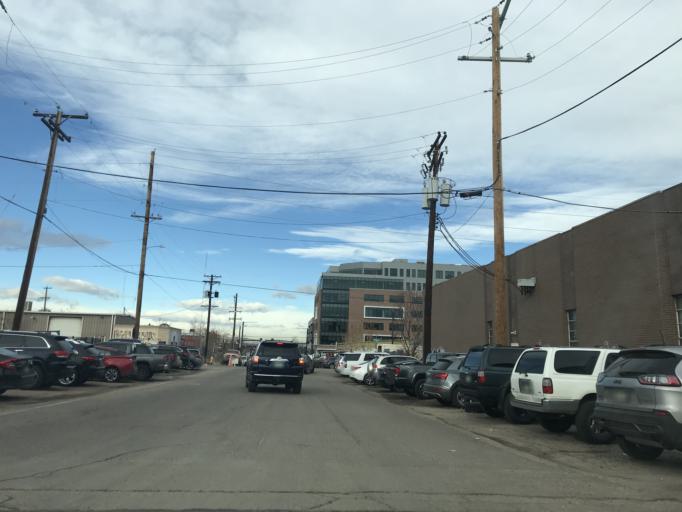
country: US
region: Colorado
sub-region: Denver County
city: Denver
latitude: 39.7693
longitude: -104.9775
